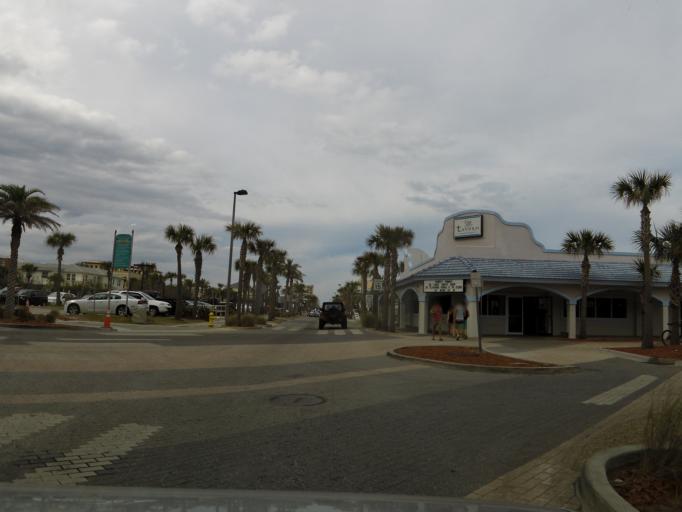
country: US
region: Florida
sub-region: Duval County
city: Jacksonville Beach
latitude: 30.2921
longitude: -81.3902
